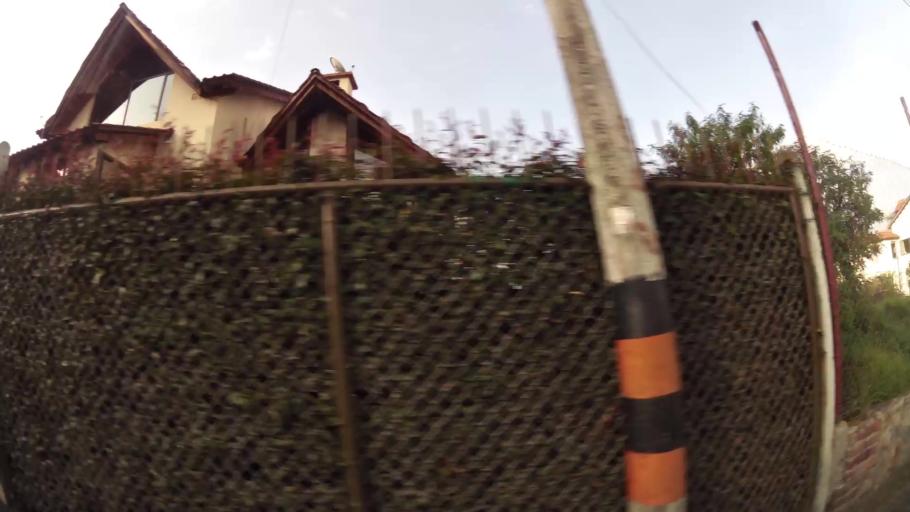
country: CO
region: Cundinamarca
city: Cota
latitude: 4.8141
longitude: -74.1064
